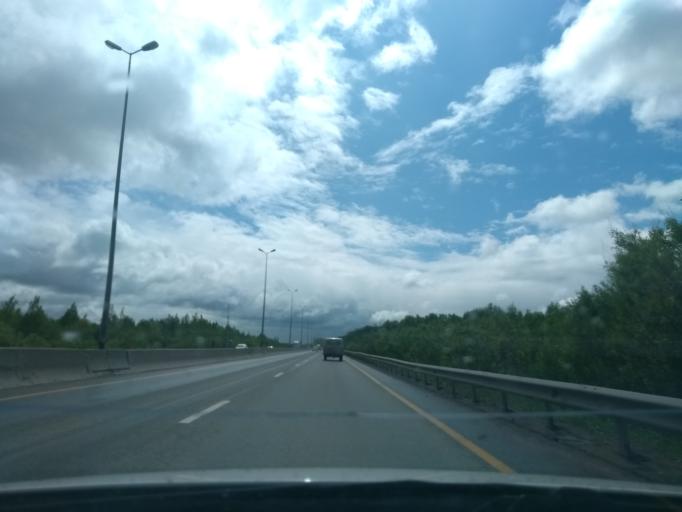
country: RU
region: Perm
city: Kondratovo
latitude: 57.9913
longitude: 56.0639
